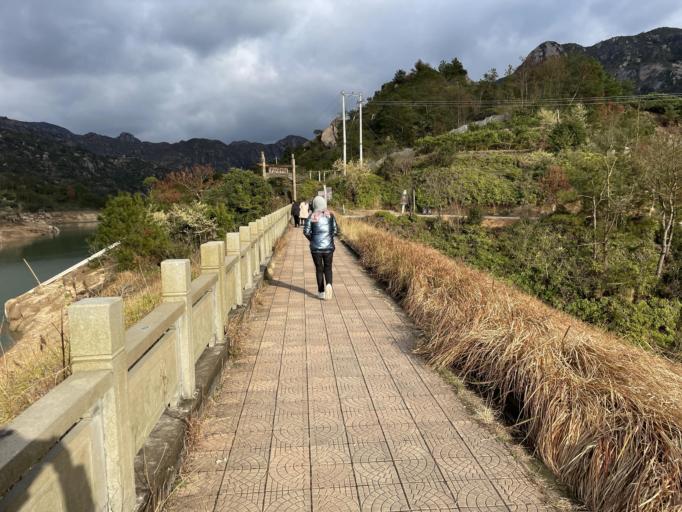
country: CN
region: Zhejiang Sheng
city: Wenzhou
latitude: 27.8759
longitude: 120.7113
